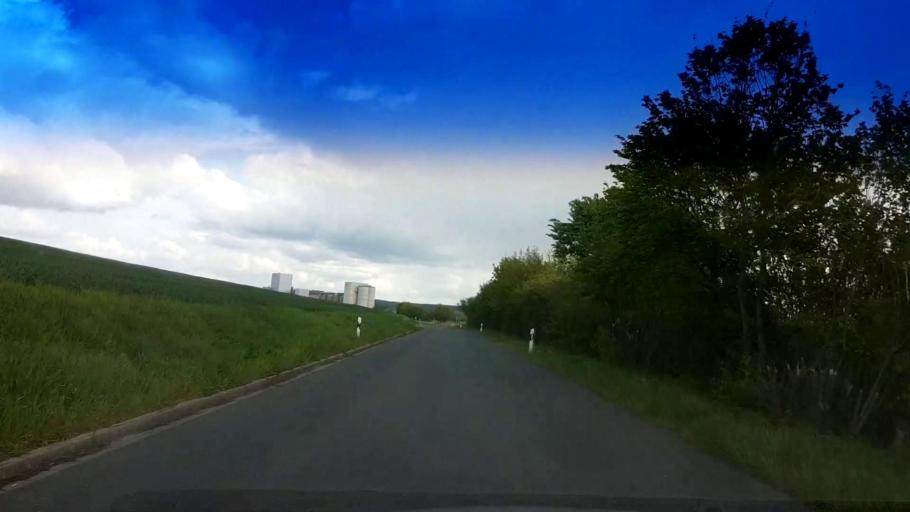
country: DE
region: Bavaria
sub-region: Upper Franconia
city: Pommersfelden
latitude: 49.7826
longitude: 10.8268
